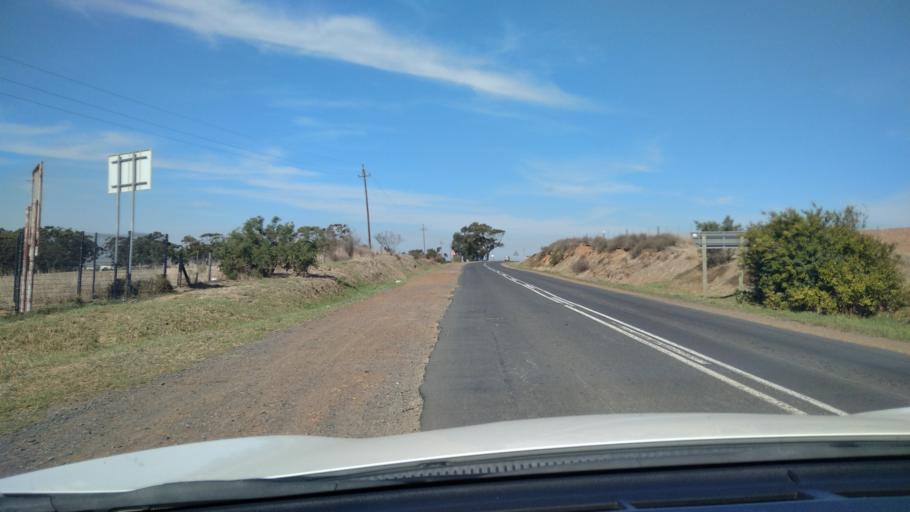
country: ZA
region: Western Cape
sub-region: City of Cape Town
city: Atlantis
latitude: -33.6681
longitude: 18.5820
